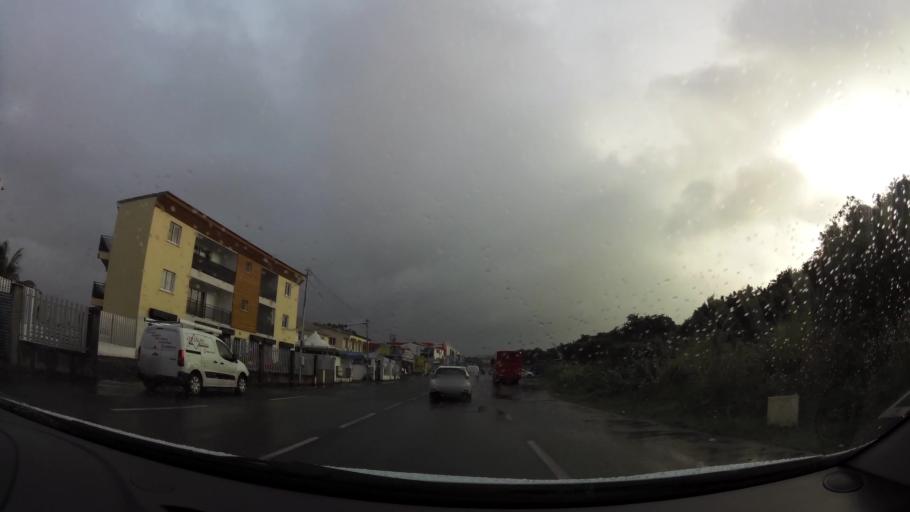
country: RE
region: Reunion
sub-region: Reunion
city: Saint-Andre
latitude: -20.9599
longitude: 55.6630
